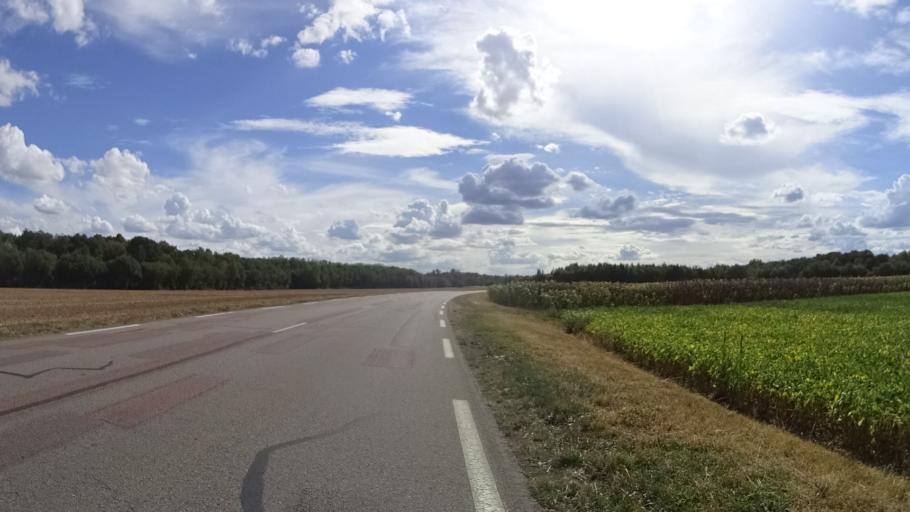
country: FR
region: Bourgogne
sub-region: Departement de la Cote-d'Or
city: Seurre
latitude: 47.0398
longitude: 5.1861
